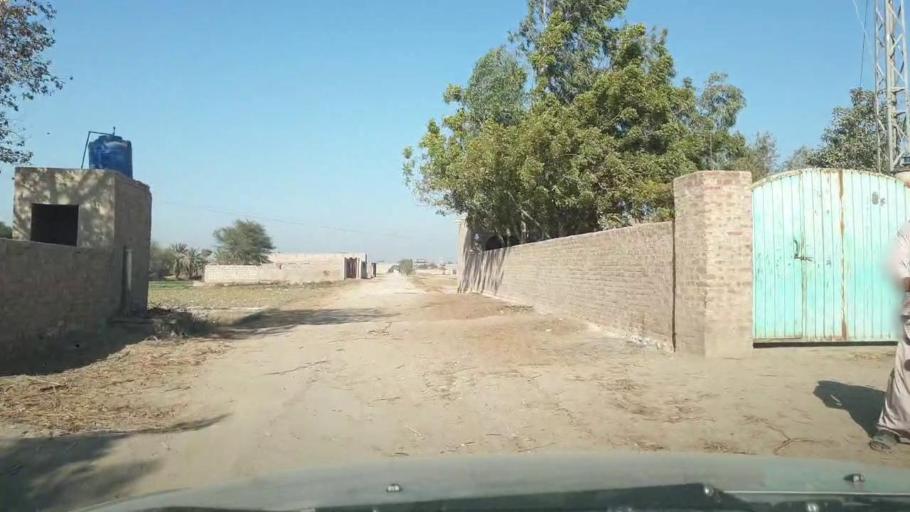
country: PK
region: Sindh
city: Ghotki
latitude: 28.0493
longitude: 69.3371
